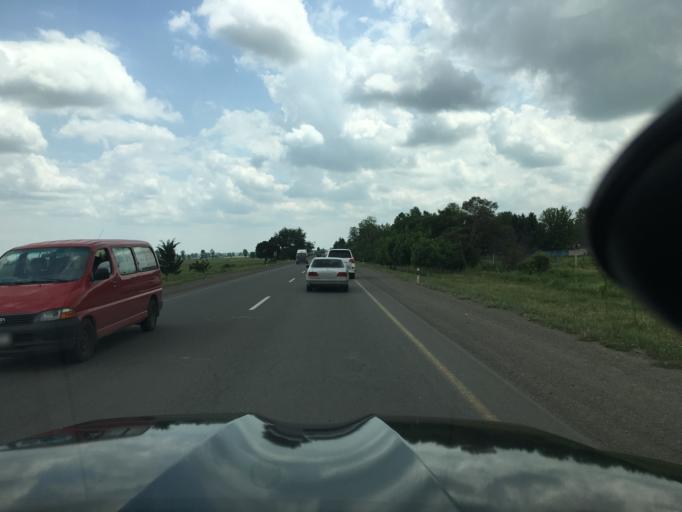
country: AZ
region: Tovuz
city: Tovuz
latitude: 40.9610
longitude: 45.7196
